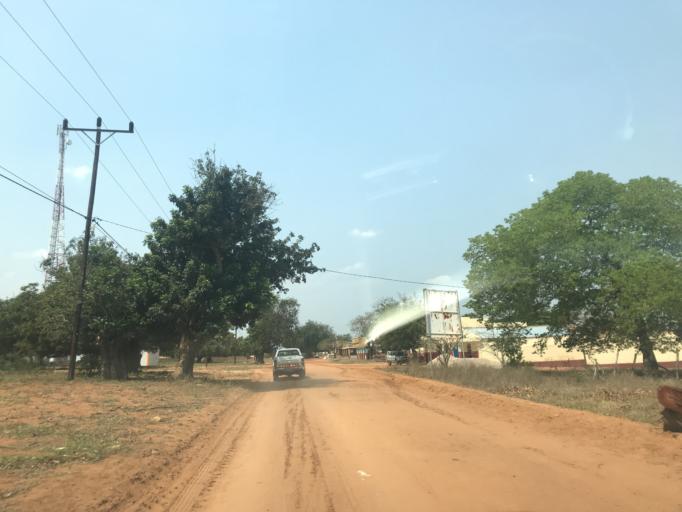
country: MZ
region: Gaza
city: Manjacaze
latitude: -24.4893
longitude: 33.9595
